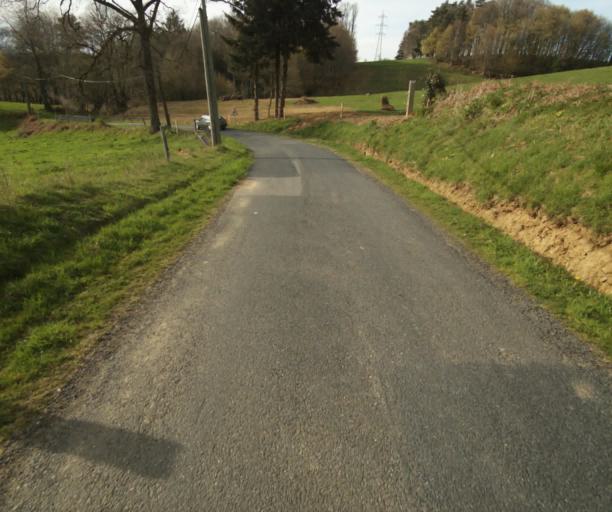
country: FR
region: Limousin
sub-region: Departement de la Correze
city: Naves
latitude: 45.3156
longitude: 1.7457
